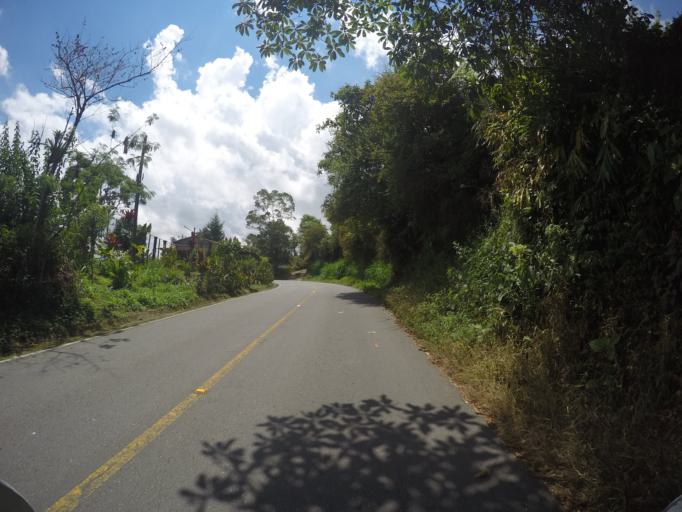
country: CO
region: Quindio
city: Filandia
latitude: 4.6454
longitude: -75.6821
